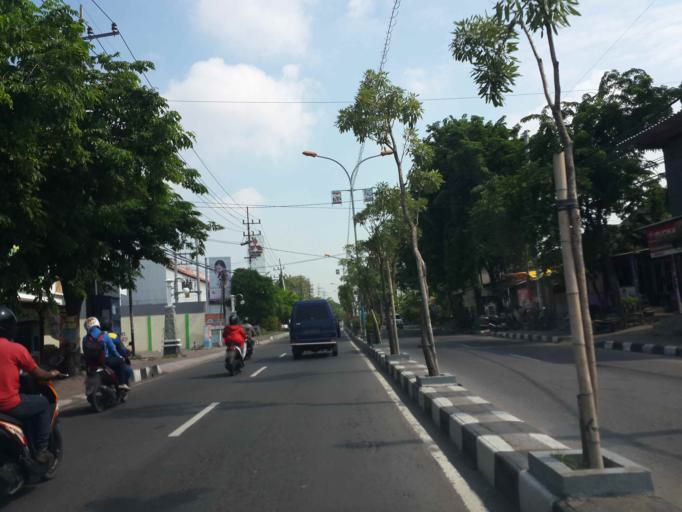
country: ID
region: East Java
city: Kebomas
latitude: -7.1839
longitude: 112.6485
